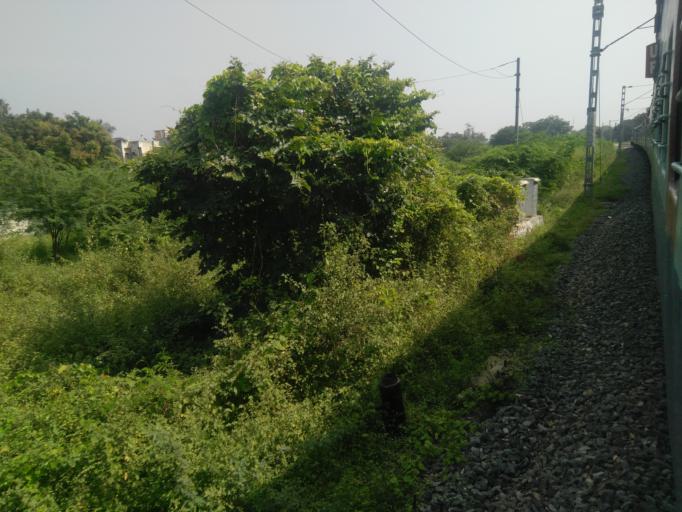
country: IN
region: Tamil Nadu
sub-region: Coimbatore
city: Karamadai
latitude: 11.2414
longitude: 76.9566
